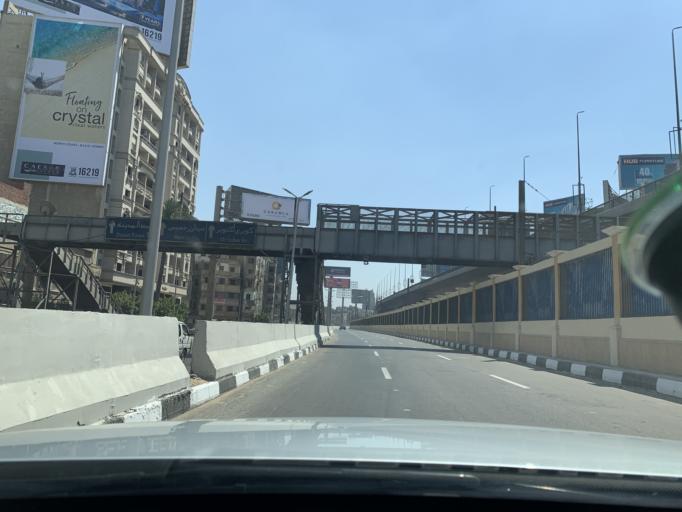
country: EG
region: Muhafazat al Qahirah
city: Cairo
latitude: 30.0735
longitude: 31.2713
